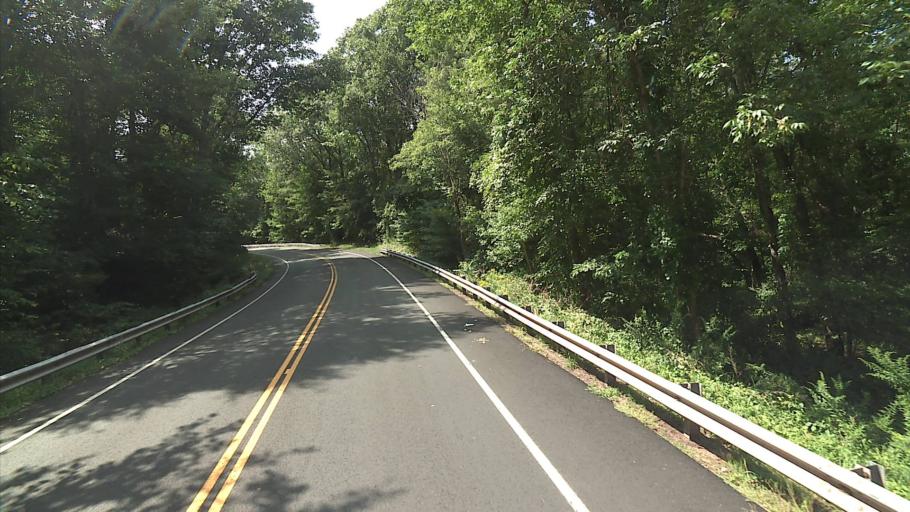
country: US
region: Connecticut
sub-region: Hartford County
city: Broad Brook
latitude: 41.9122
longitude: -72.5606
